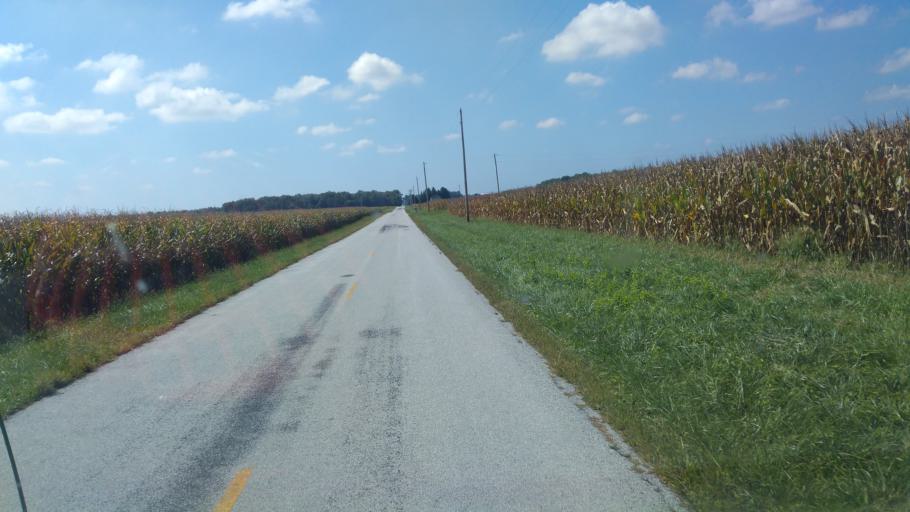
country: US
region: Ohio
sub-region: Hardin County
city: Ada
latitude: 40.7477
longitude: -83.7261
